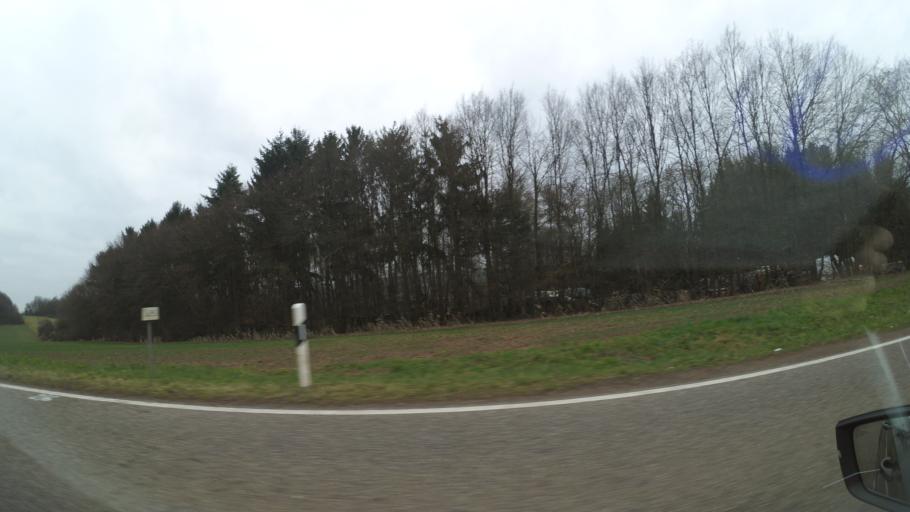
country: DE
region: Saarland
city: Heusweiler
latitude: 49.3540
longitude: 6.9713
